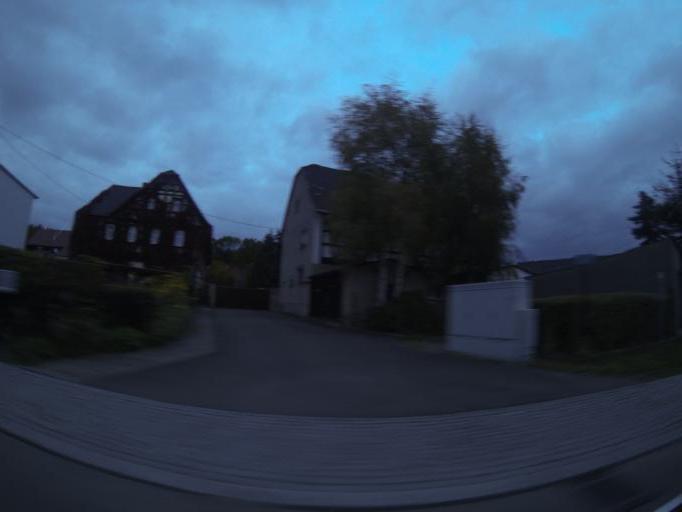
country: DE
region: Thuringia
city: Saara
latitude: 50.9229
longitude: 12.3878
